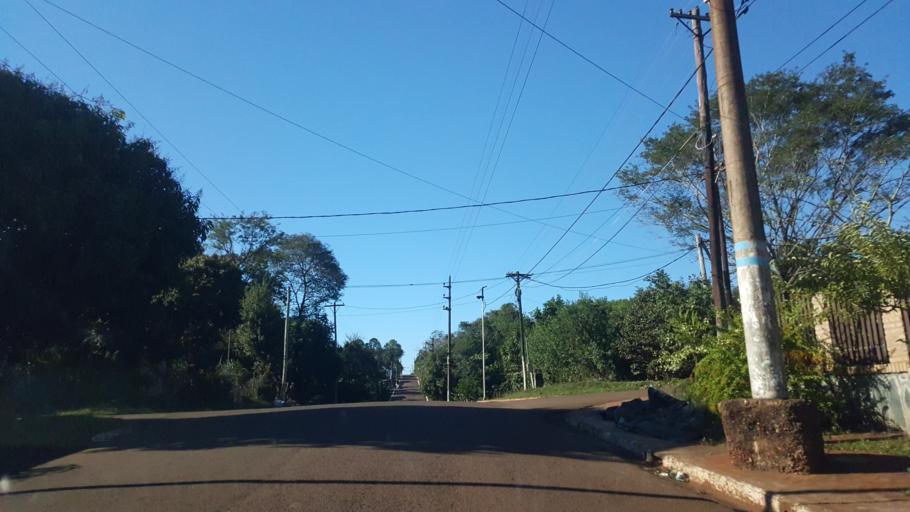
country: AR
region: Misiones
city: Gobernador Roca
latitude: -27.1948
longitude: -55.4723
